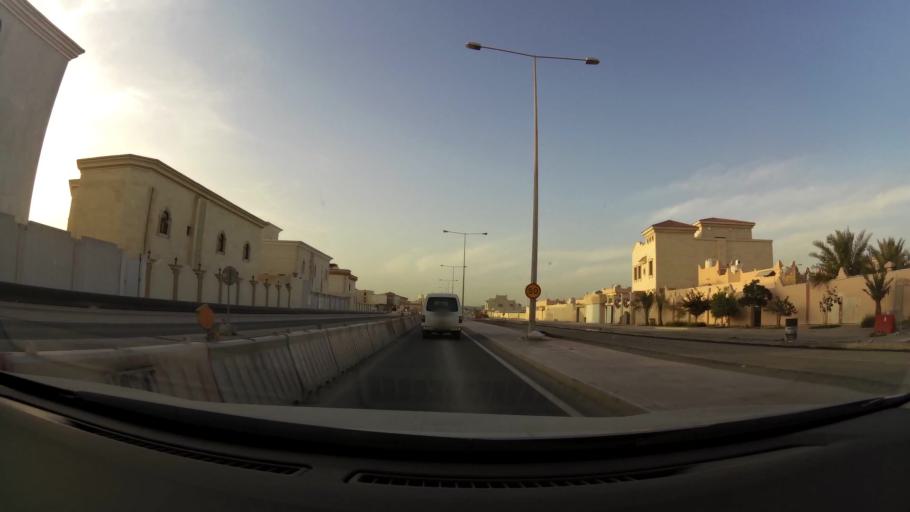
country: QA
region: Al Wakrah
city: Al Wakrah
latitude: 25.1588
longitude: 51.5917
